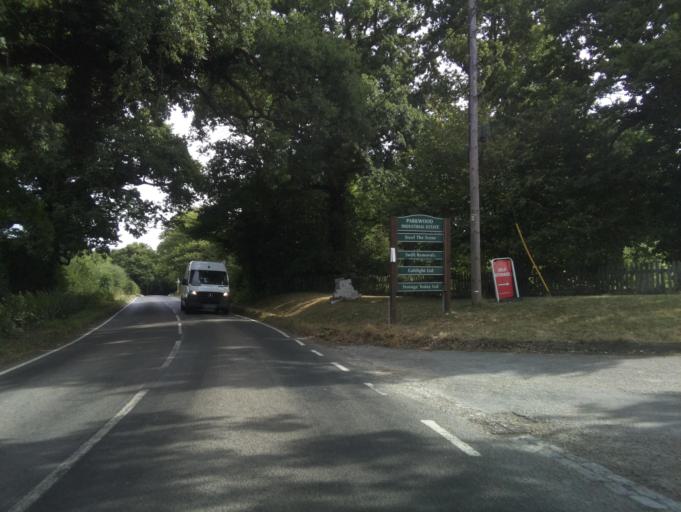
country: GB
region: England
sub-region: Surrey
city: Godstone
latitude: 51.1925
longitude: -0.0662
